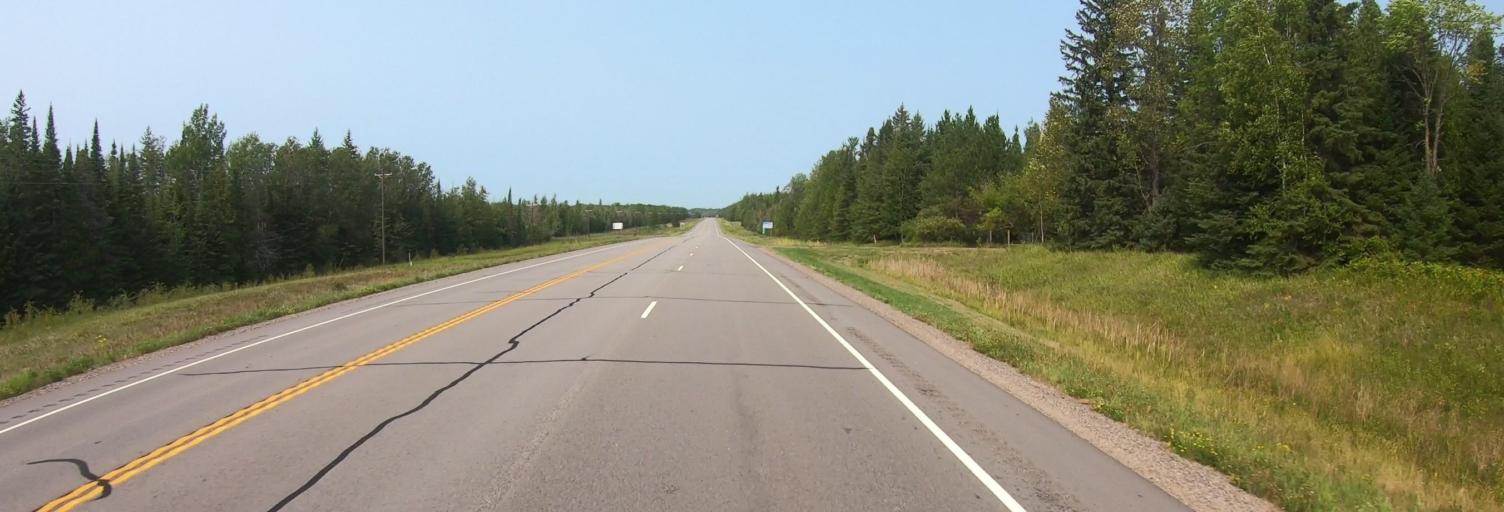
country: CA
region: Ontario
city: Fort Frances
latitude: 48.4021
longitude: -93.0226
